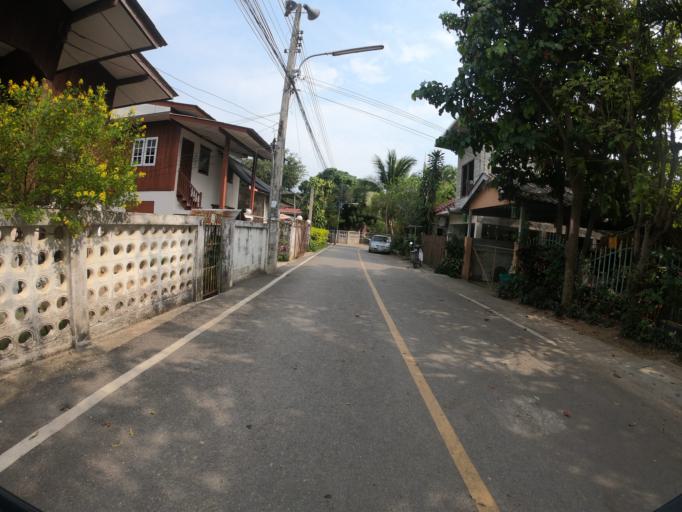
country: TH
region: Chiang Mai
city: Hang Dong
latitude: 18.7464
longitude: 98.9391
